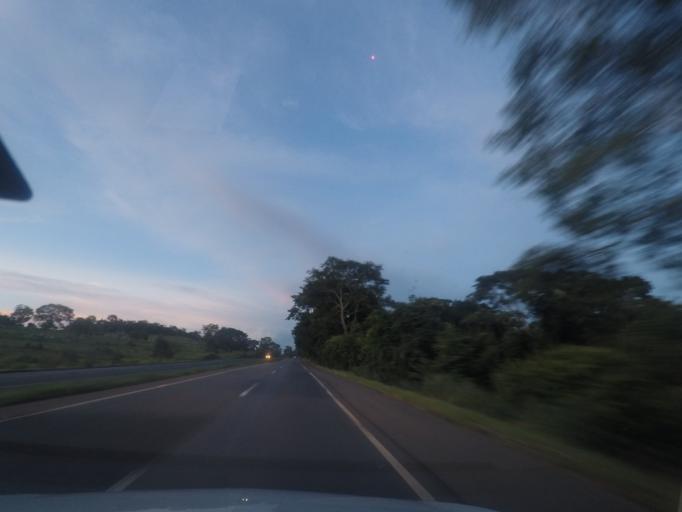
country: BR
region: Goias
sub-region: Pontalina
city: Pontalina
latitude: -17.4906
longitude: -49.2120
